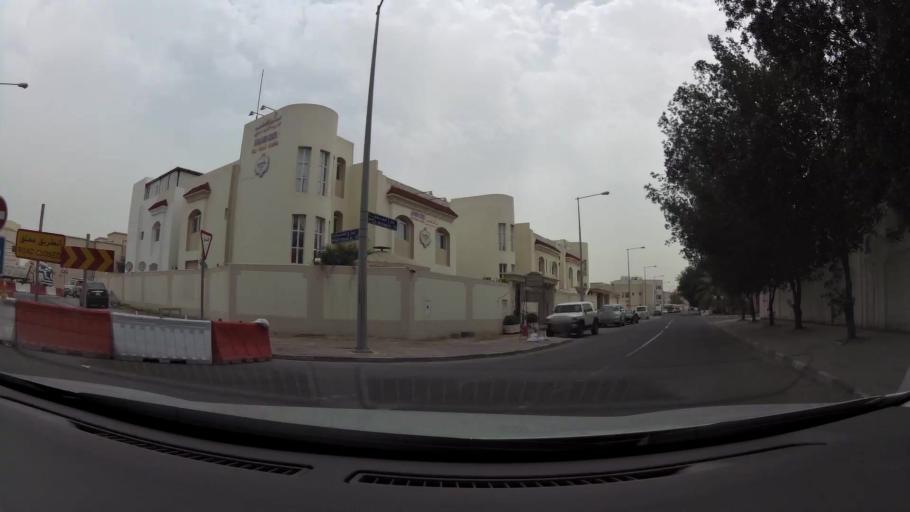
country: QA
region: Baladiyat ad Dawhah
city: Doha
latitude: 25.2592
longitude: 51.5110
